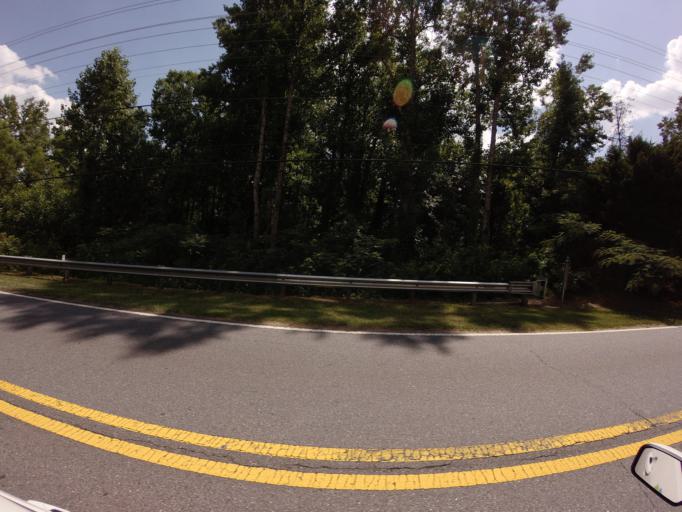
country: US
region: Georgia
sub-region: Fulton County
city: Johns Creek
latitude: 34.0206
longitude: -84.2460
